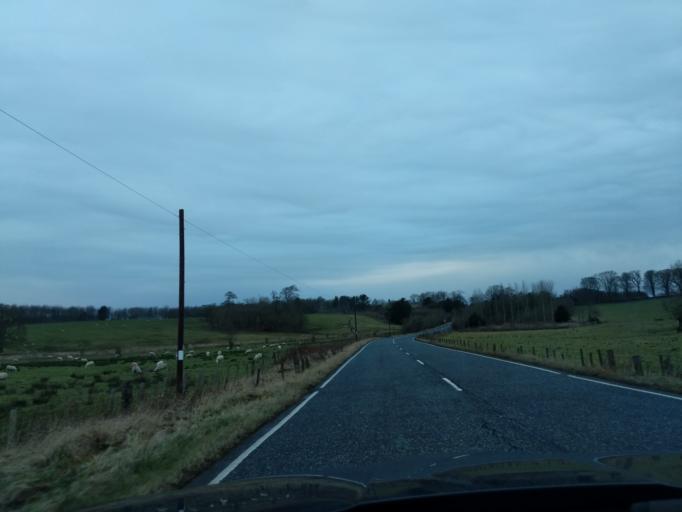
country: GB
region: England
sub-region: Northumberland
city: Rothley
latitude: 55.1412
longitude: -1.9852
